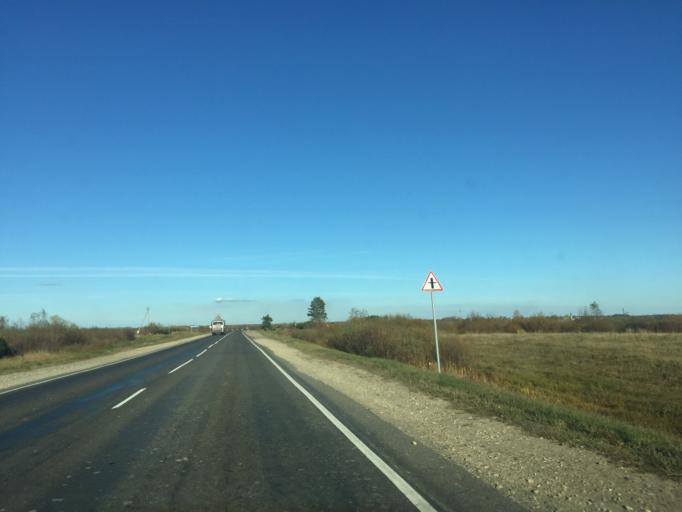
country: BY
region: Vitebsk
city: Dzisna
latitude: 55.3404
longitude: 28.2898
